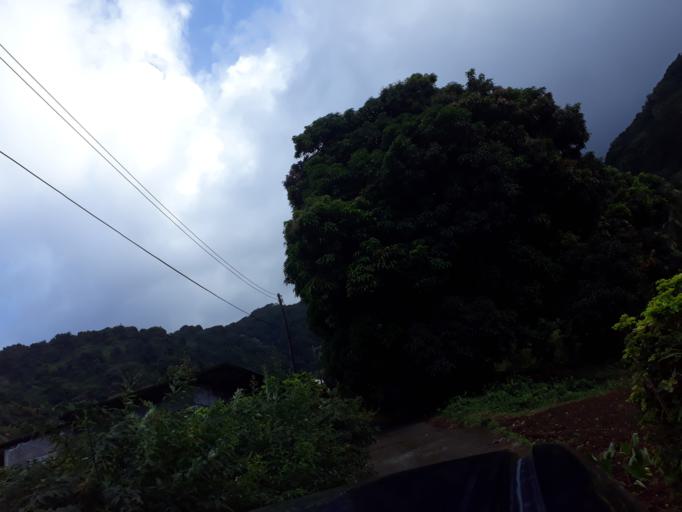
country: VC
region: Charlotte
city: Georgetown
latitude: 13.3784
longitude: -61.1705
